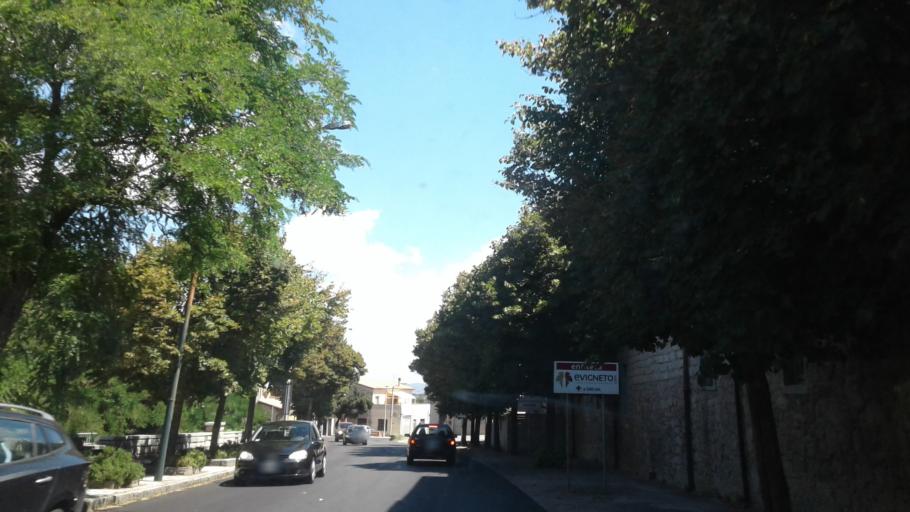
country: IT
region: Sardinia
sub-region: Provincia di Olbia-Tempio
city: Tempio Pausania
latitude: 40.9027
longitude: 9.1097
